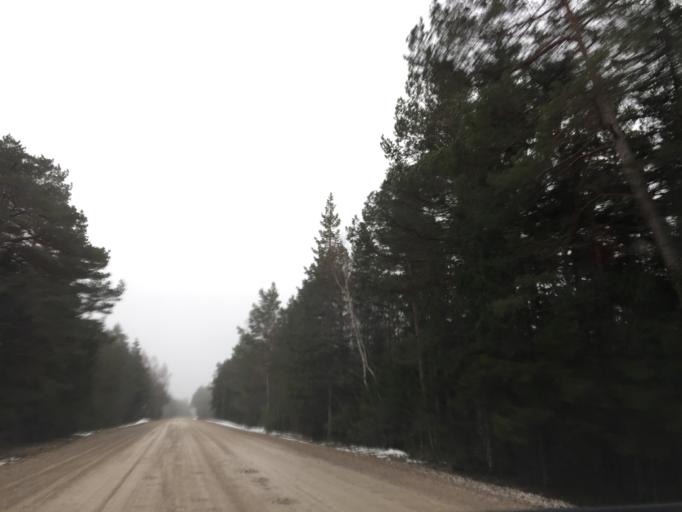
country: EE
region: Saare
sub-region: Kuressaare linn
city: Kuressaare
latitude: 58.4801
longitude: 21.9999
